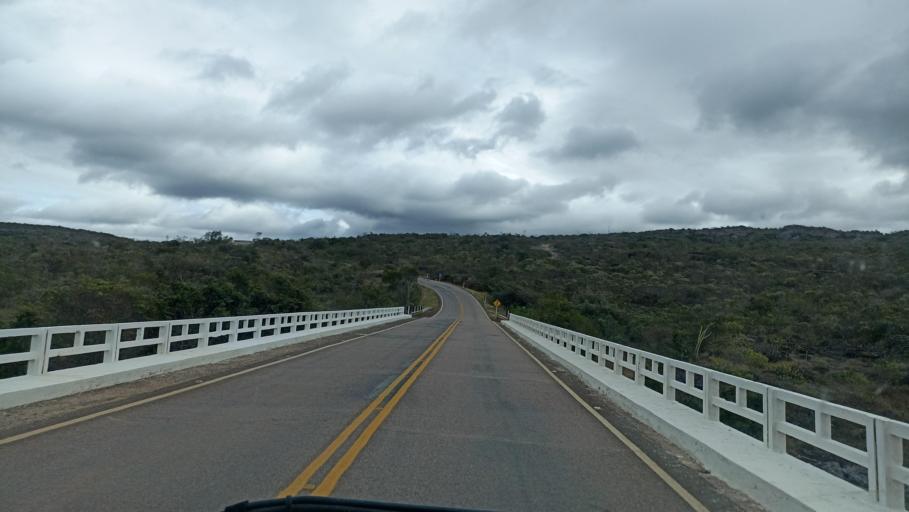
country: BR
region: Bahia
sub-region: Andarai
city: Vera Cruz
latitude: -12.9908
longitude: -41.3502
